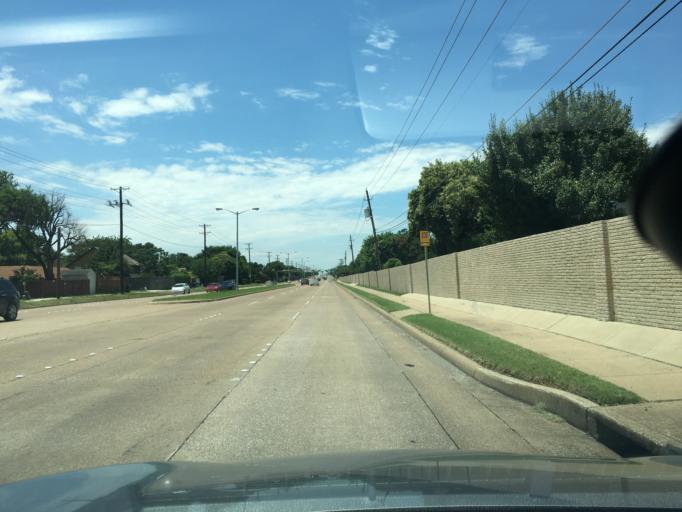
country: US
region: Texas
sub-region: Dallas County
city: Richardson
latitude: 32.9313
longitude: -96.6878
